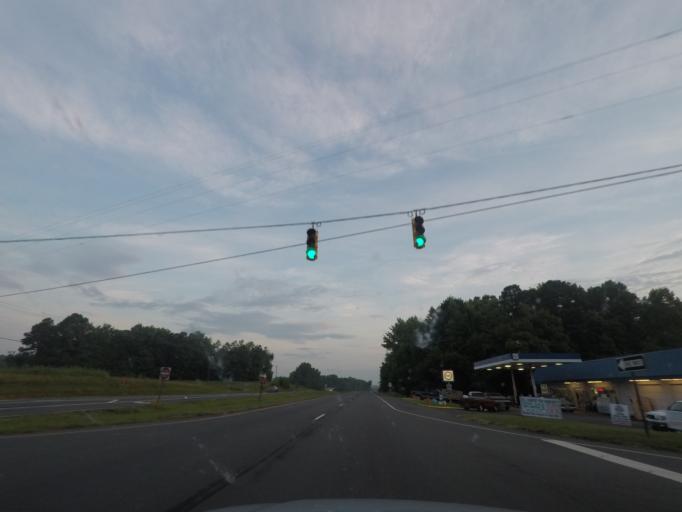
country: US
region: North Carolina
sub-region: Person County
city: Roxboro
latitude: 36.2829
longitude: -78.9566
